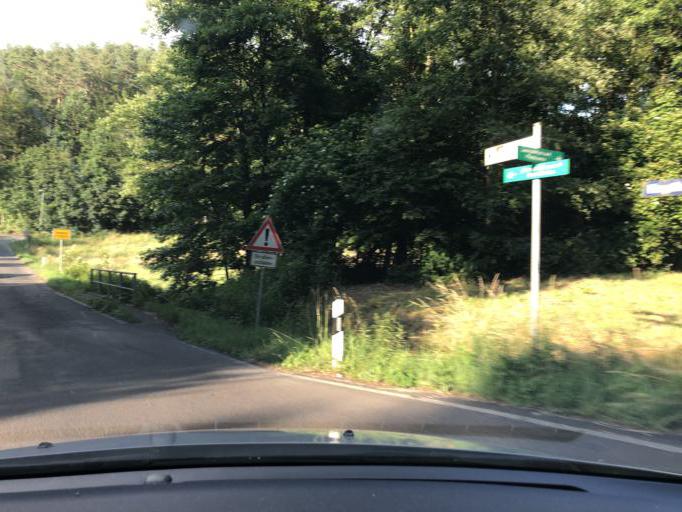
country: DE
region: Saxony
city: Bannewitz
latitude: 50.9849
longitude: 13.6970
